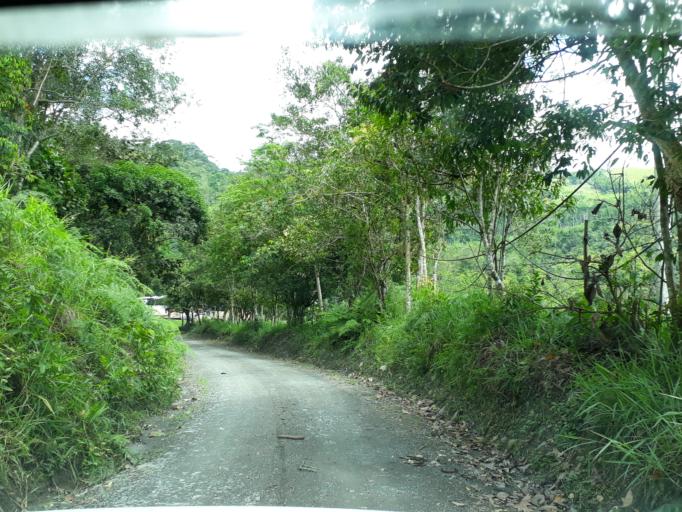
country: CO
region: Boyaca
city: Quipama
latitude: 5.4422
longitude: -74.1806
